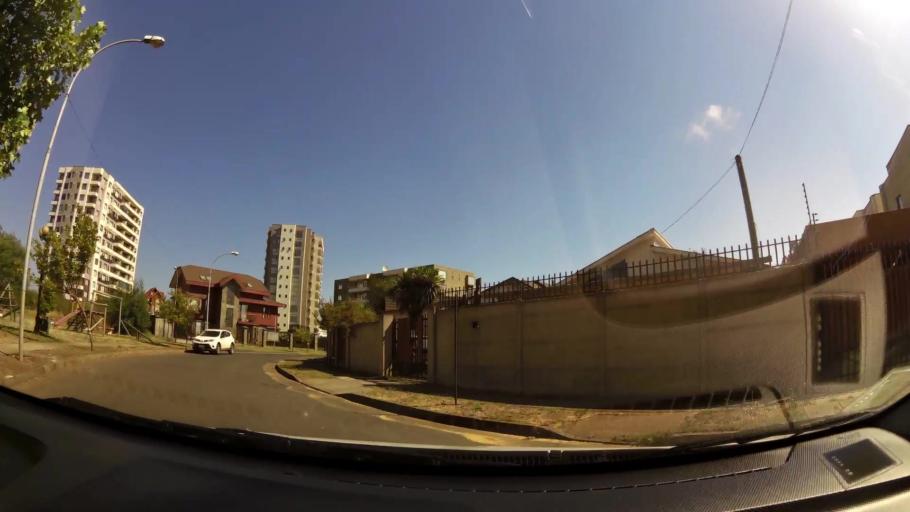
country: CL
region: Biobio
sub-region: Provincia de Concepcion
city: Concepcion
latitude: -36.7832
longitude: -73.0467
